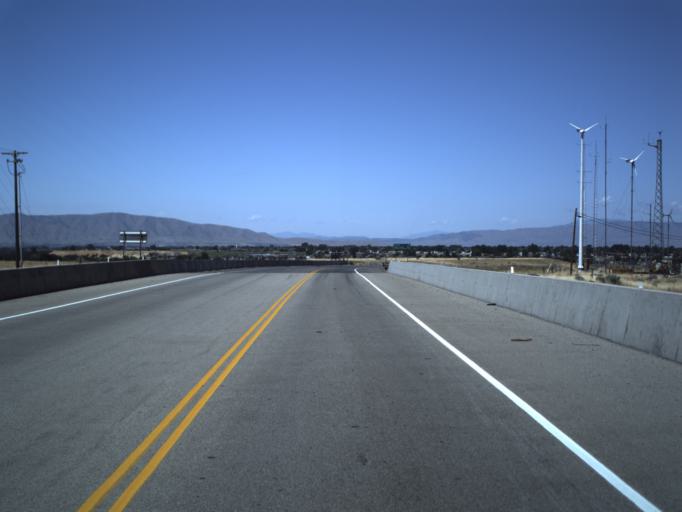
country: US
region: Utah
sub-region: Utah County
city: Mapleton
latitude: 40.0824
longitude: -111.5884
